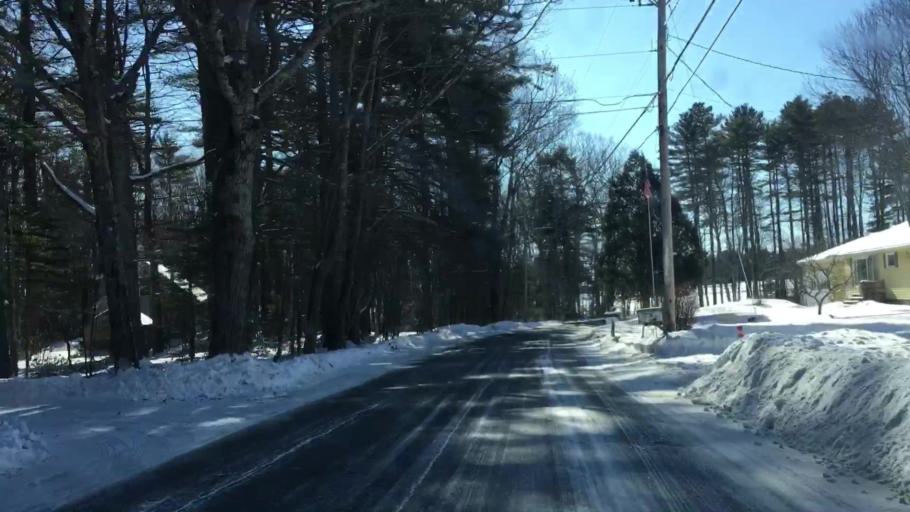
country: US
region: Maine
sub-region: Cumberland County
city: Brunswick
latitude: 43.8937
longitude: -69.9984
